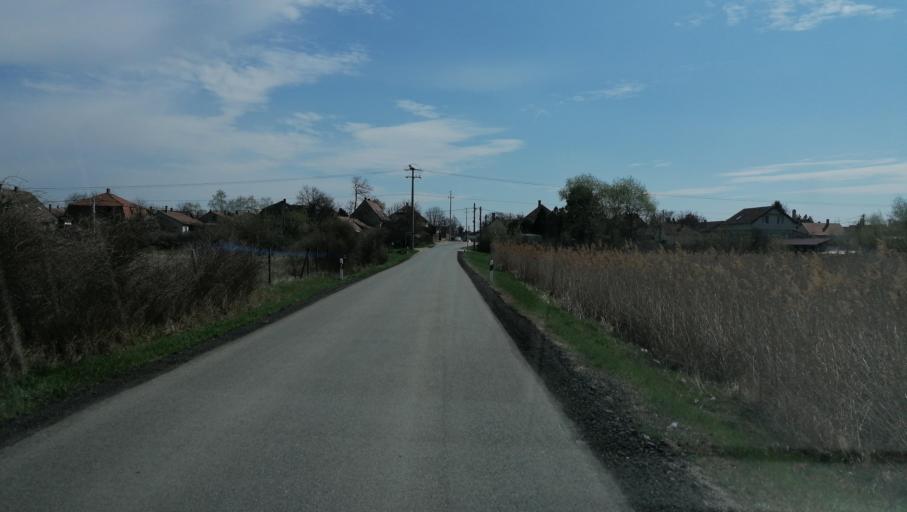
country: HU
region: Pest
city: Kiskunlachaza
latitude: 47.1894
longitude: 18.9999
